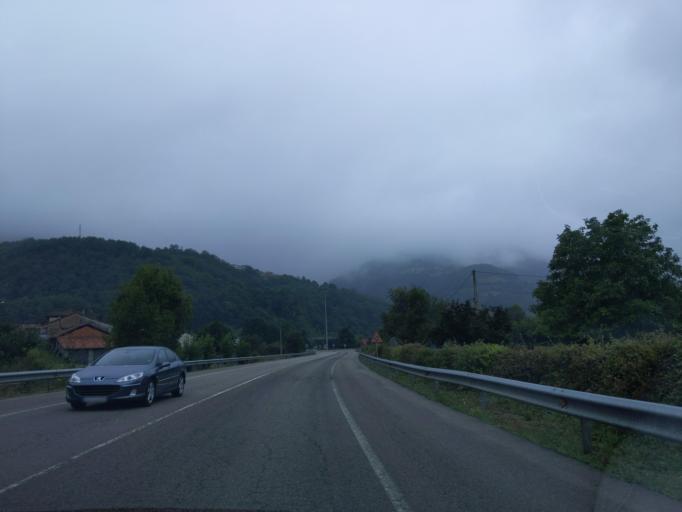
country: ES
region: Asturias
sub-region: Province of Asturias
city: Pola de Laviana
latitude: 43.2352
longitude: -5.5534
